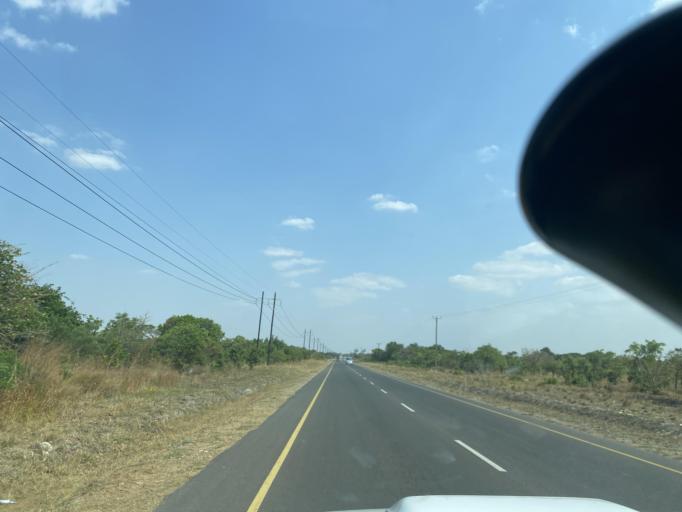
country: ZM
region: Lusaka
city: Lusaka
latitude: -15.3262
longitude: 28.0671
